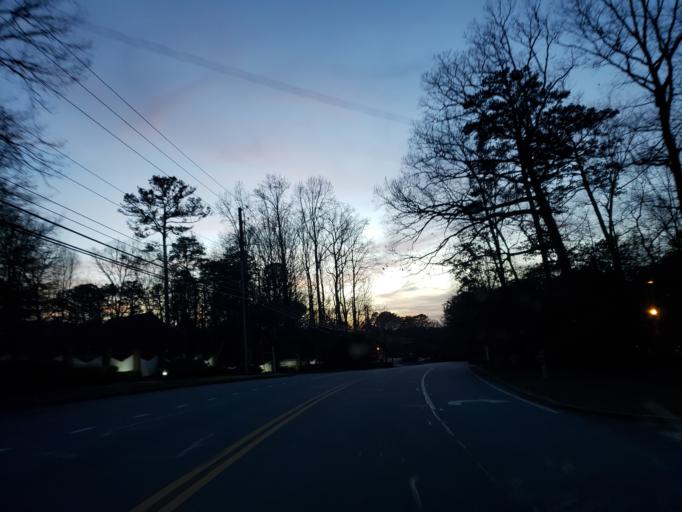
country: US
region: Georgia
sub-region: DeKalb County
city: North Druid Hills
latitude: 33.8256
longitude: -84.2836
